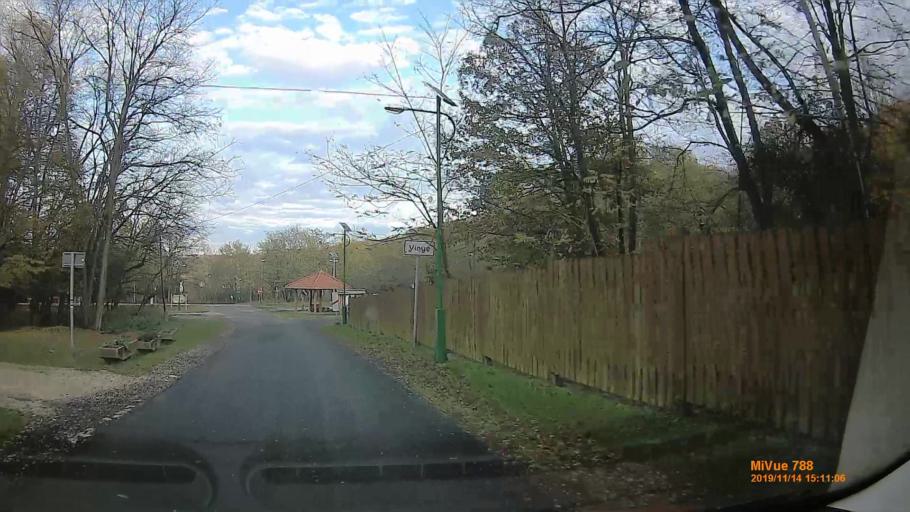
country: HU
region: Gyor-Moson-Sopron
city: Bakonyszentlaszlo
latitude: 47.3597
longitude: 17.8188
